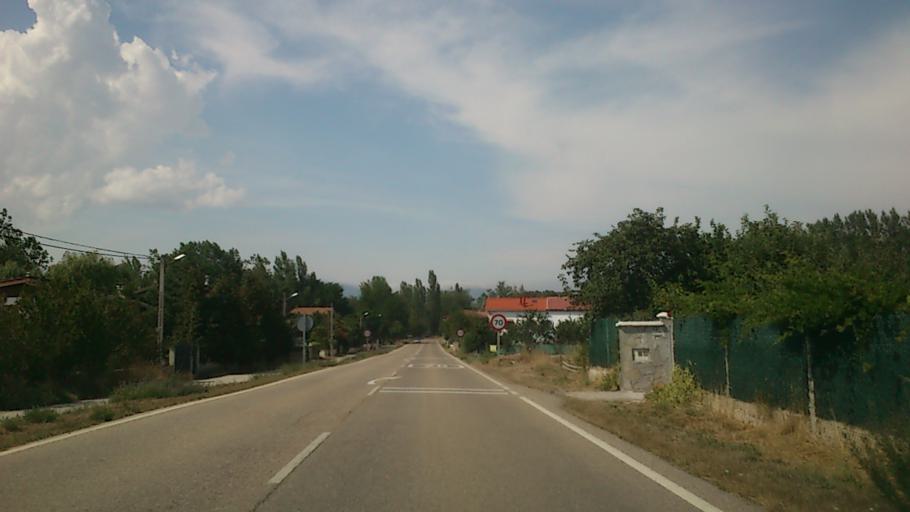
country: ES
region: Castille and Leon
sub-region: Provincia de Burgos
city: Medina de Pomar
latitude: 43.0125
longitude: -3.4828
